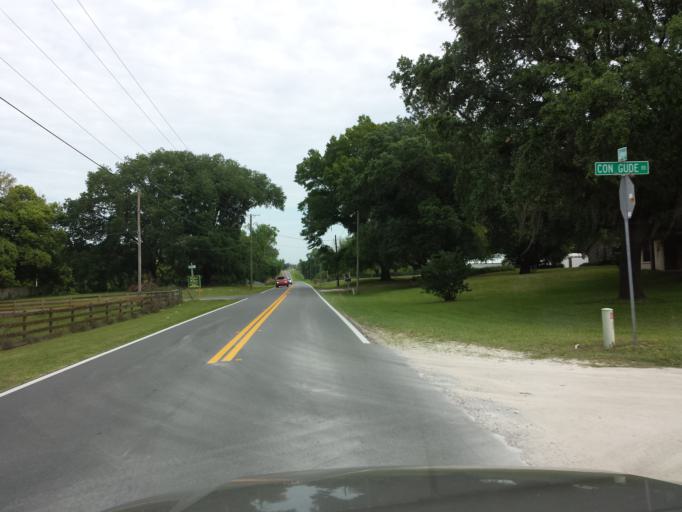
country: US
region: Florida
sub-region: Pasco County
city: San Antonio
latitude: 28.3614
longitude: -82.2744
